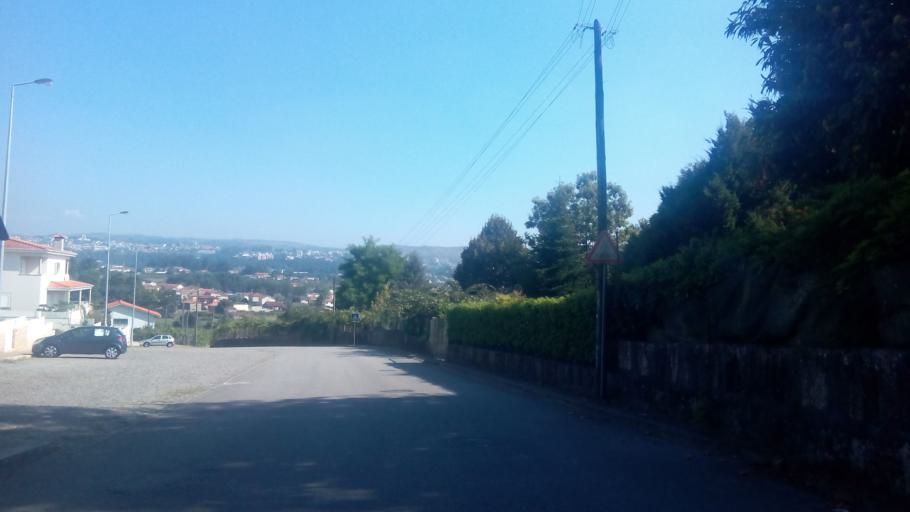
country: PT
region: Porto
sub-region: Paredes
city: Madalena
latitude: 41.2157
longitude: -8.3349
